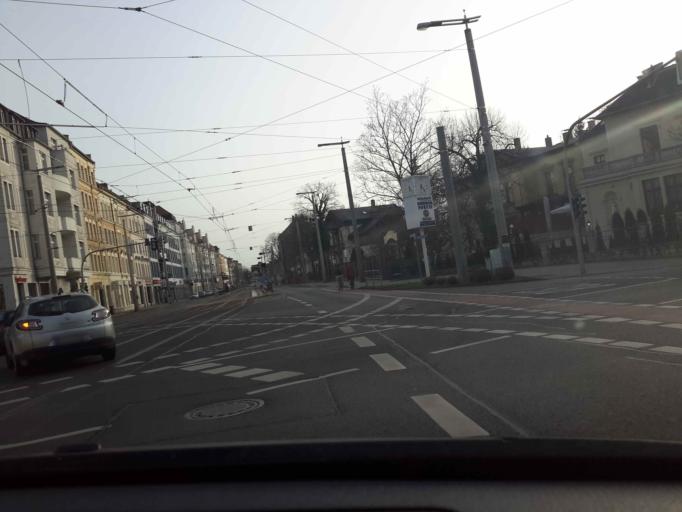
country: DE
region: Saxony
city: Leipzig
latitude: 51.3658
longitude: 12.3853
